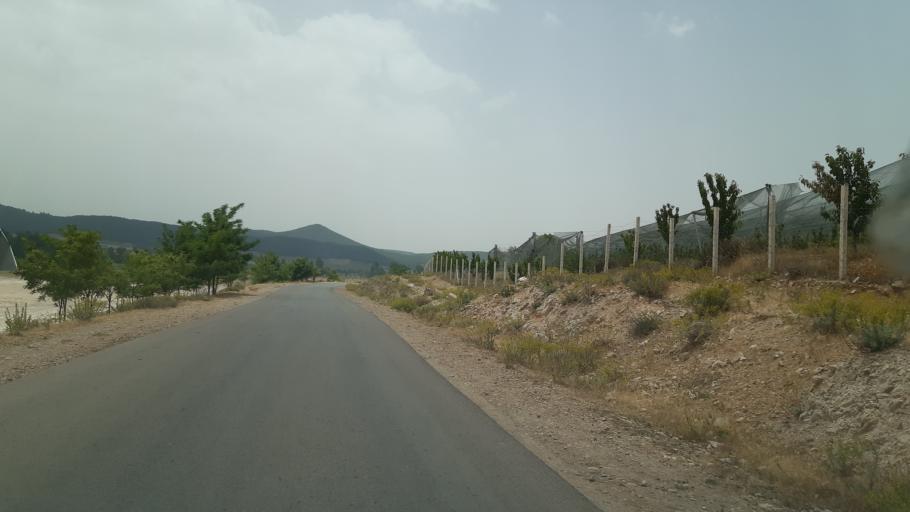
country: MA
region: Meknes-Tafilalet
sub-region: Ifrane
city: Ifrane
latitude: 33.6534
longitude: -5.0143
